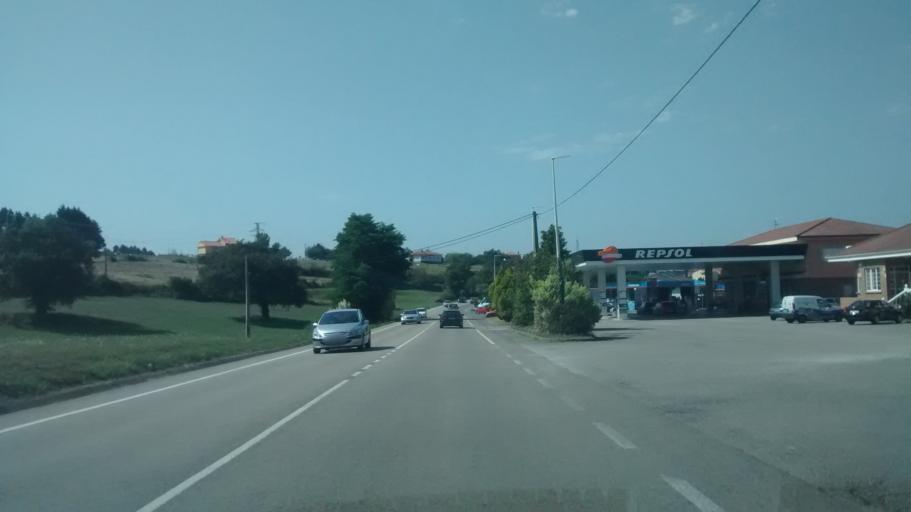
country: ES
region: Cantabria
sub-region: Provincia de Cantabria
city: Arnuero
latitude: 43.4502
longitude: -3.5583
